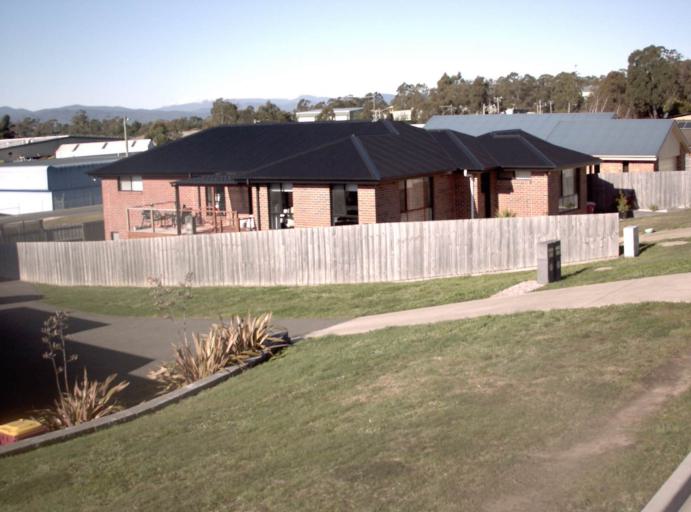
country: AU
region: Tasmania
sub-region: Launceston
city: Summerhill
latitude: -41.4720
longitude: 147.1335
